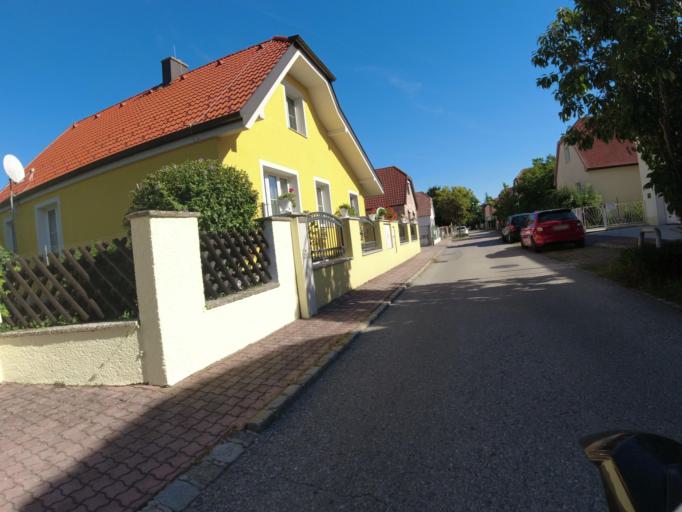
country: AT
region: Lower Austria
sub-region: Politischer Bezirk Modling
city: Guntramsdorf
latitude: 48.0184
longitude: 16.3231
